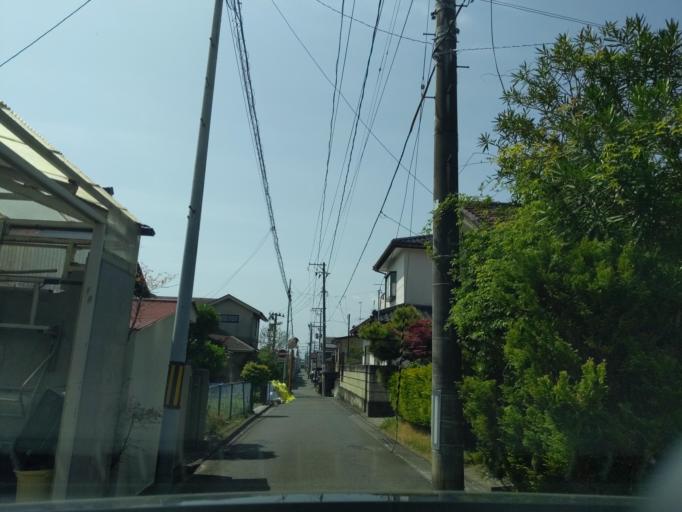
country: JP
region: Fukushima
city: Koriyama
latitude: 37.3753
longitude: 140.3697
